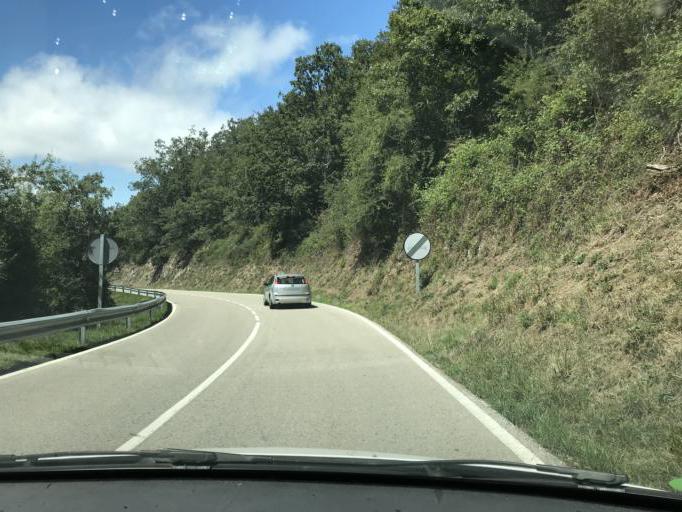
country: ES
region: Cantabria
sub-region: Provincia de Cantabria
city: Cabezon de Liebana
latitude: 43.0639
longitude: -4.4791
